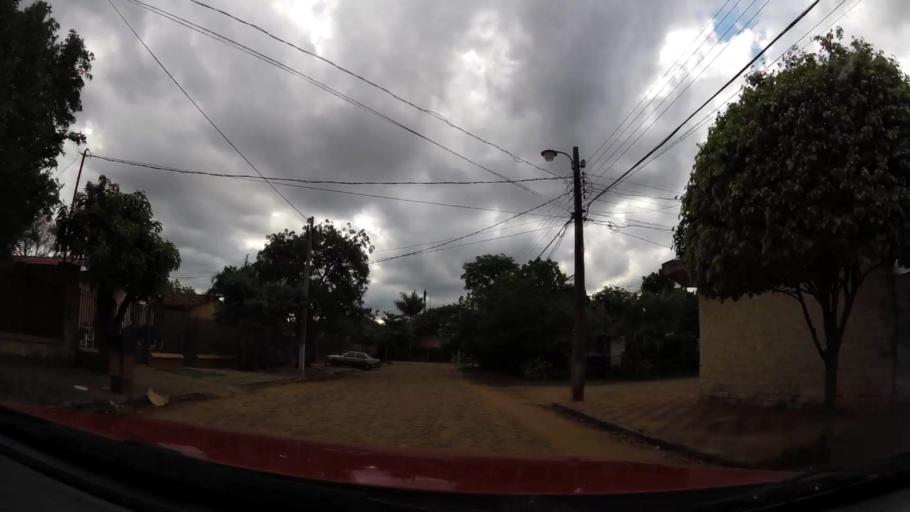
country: PY
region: Central
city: San Lorenzo
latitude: -25.2856
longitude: -57.4967
